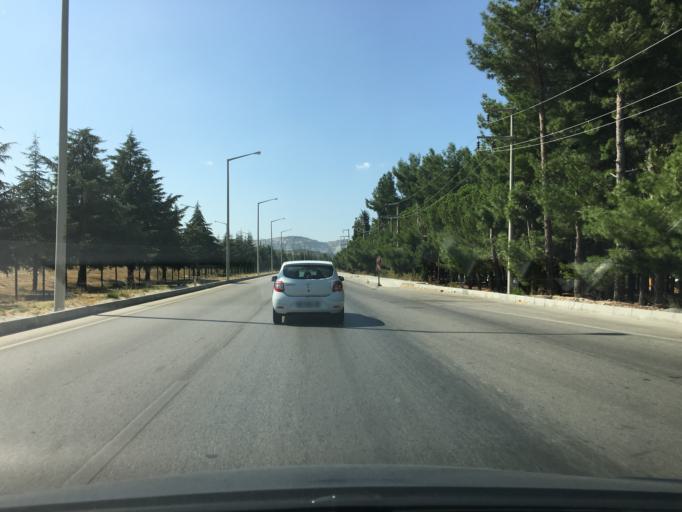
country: TR
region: Burdur
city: Burdur
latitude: 37.7358
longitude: 30.3106
